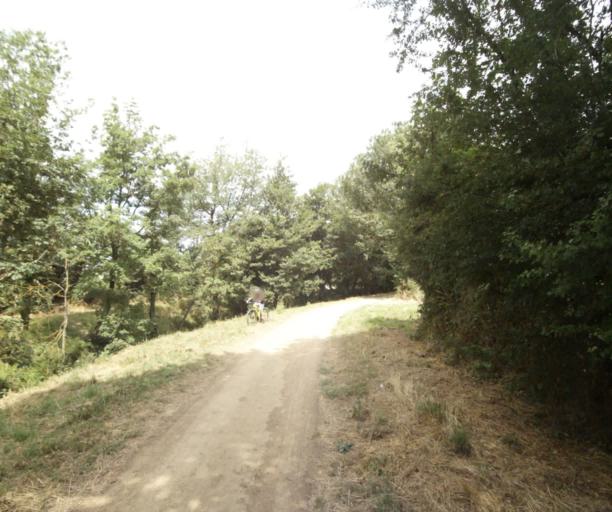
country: FR
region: Midi-Pyrenees
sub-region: Departement de la Haute-Garonne
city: Saint-Felix-Lauragais
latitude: 43.4310
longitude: 1.9139
